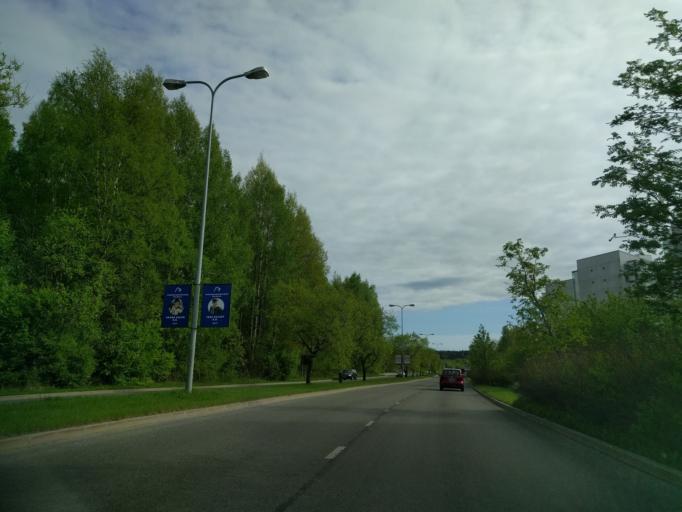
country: FI
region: Varsinais-Suomi
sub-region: Turku
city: Turku
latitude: 60.4292
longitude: 22.2403
